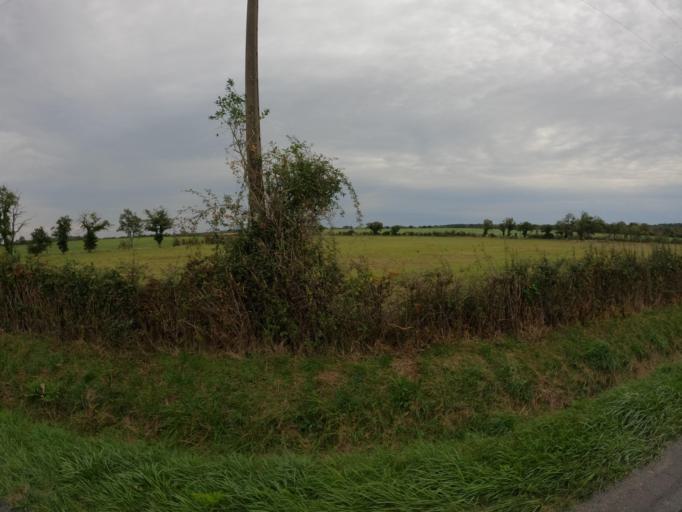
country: FR
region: Poitou-Charentes
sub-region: Departement de la Vienne
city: Saulge
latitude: 46.3636
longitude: 0.8383
